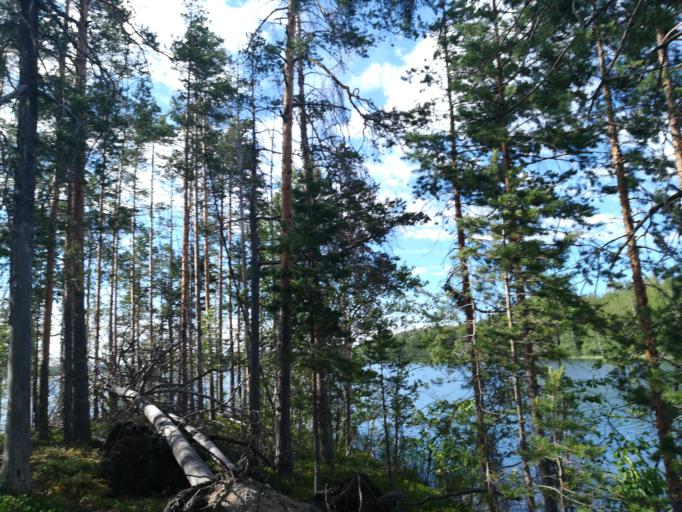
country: FI
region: Southern Savonia
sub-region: Savonlinna
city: Savonlinna
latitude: 61.6449
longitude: 28.7081
